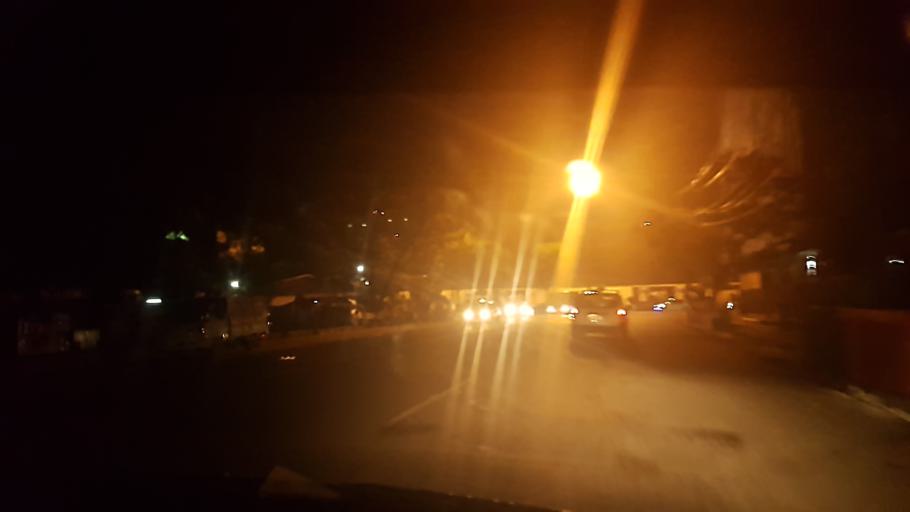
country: MM
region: Yangon
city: Yangon
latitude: 16.7699
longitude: 96.1669
